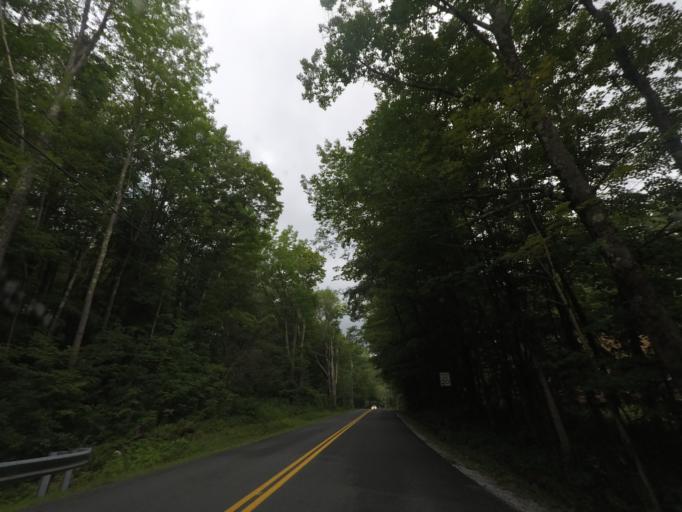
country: US
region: Massachusetts
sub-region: Berkshire County
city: Lanesborough
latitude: 42.5652
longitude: -73.2557
